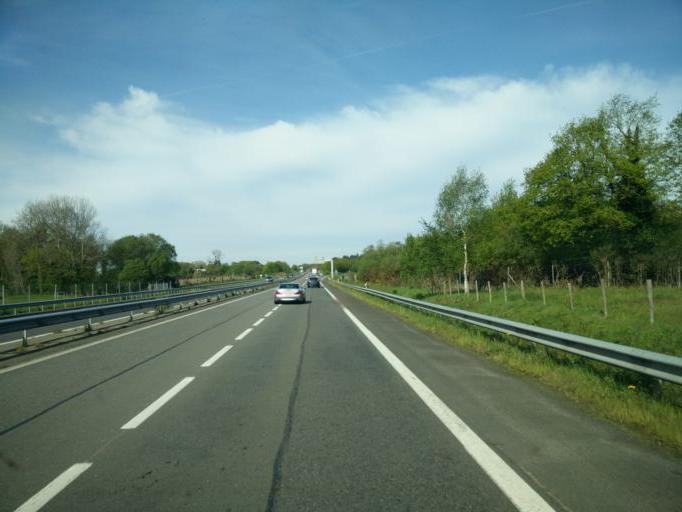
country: FR
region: Brittany
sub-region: Departement d'Ille-et-Vilaine
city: Roz-sur-Couesnon
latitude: 48.5658
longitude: -1.5977
